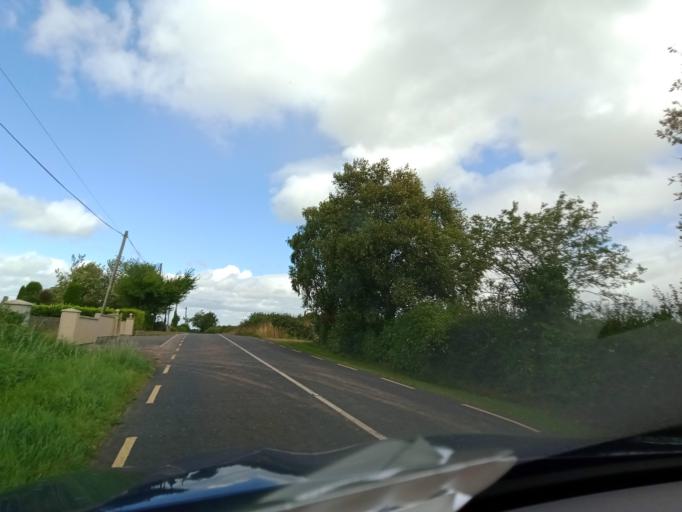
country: IE
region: Leinster
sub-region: Laois
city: Portlaoise
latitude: 52.9773
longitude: -7.2907
